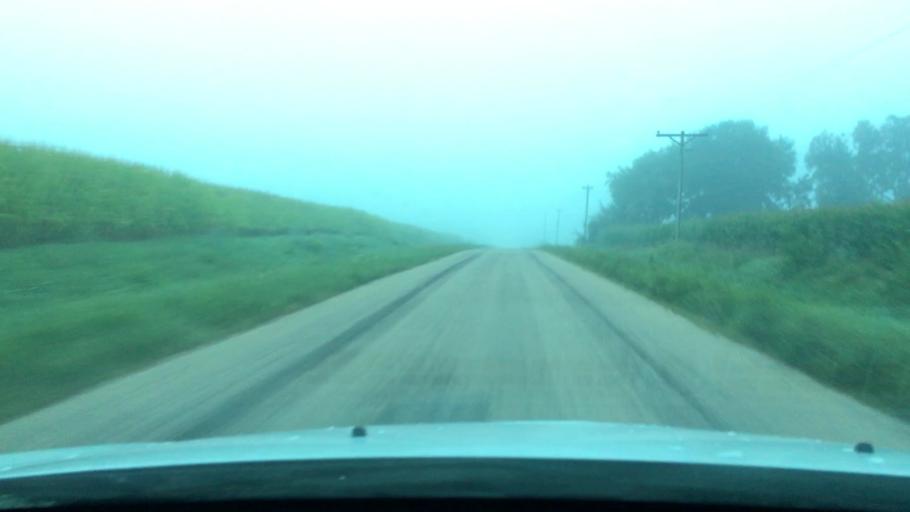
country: US
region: Illinois
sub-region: Ogle County
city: Rochelle
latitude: 41.8778
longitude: -88.9813
